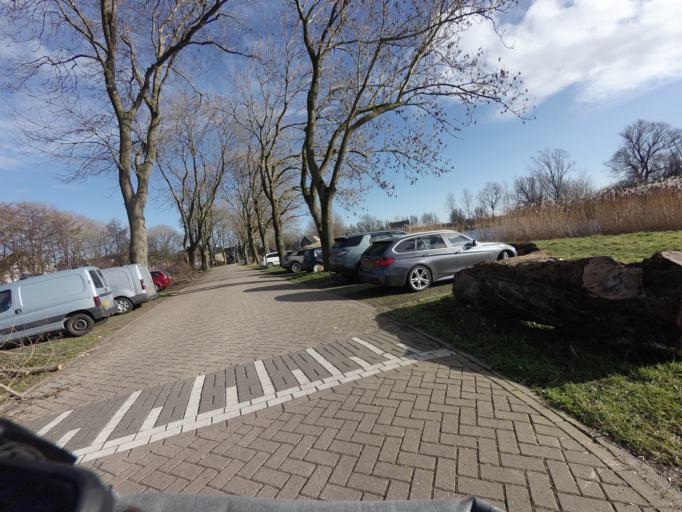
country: NL
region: North Holland
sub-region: Gemeente Uithoorn
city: Uithoorn
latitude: 52.2296
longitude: 4.8148
